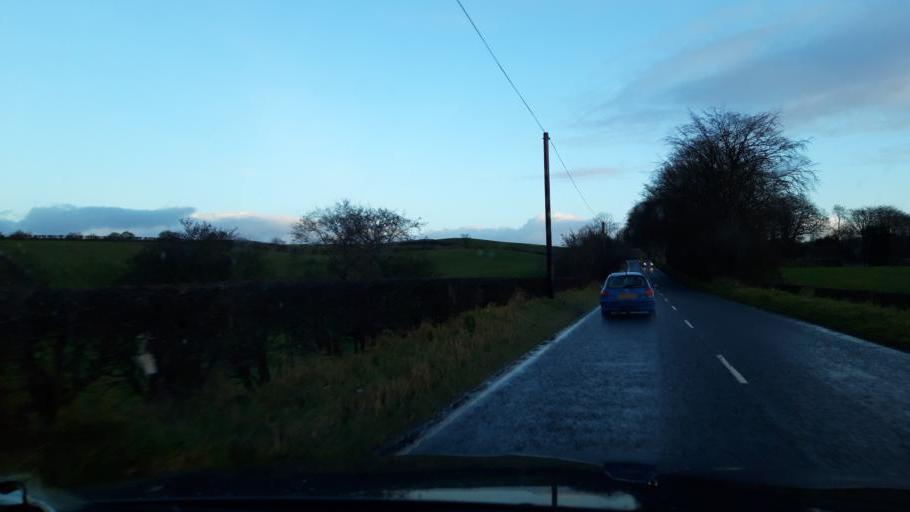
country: GB
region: Northern Ireland
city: Dunloy
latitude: 55.0355
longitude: -6.3603
